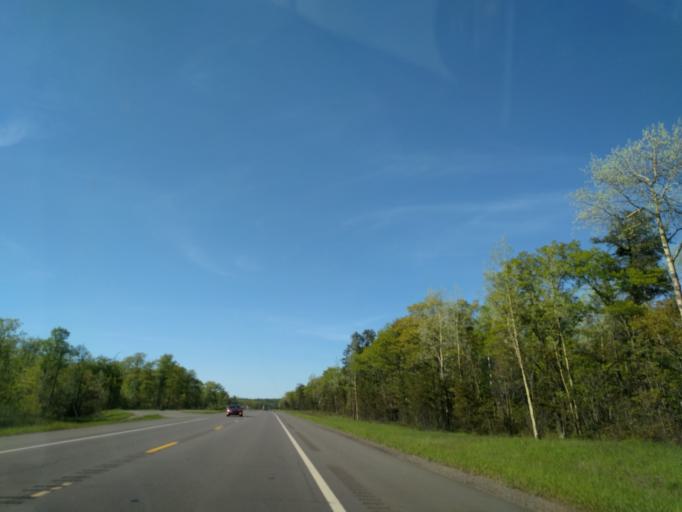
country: US
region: Michigan
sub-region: Marquette County
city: Harvey
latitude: 46.4574
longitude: -87.4255
